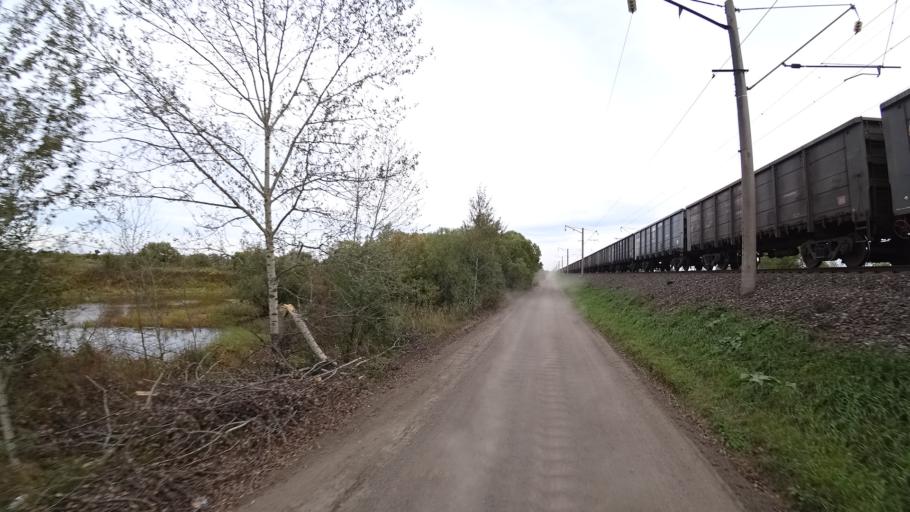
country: RU
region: Amur
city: Arkhara
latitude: 49.3627
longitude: 130.1478
